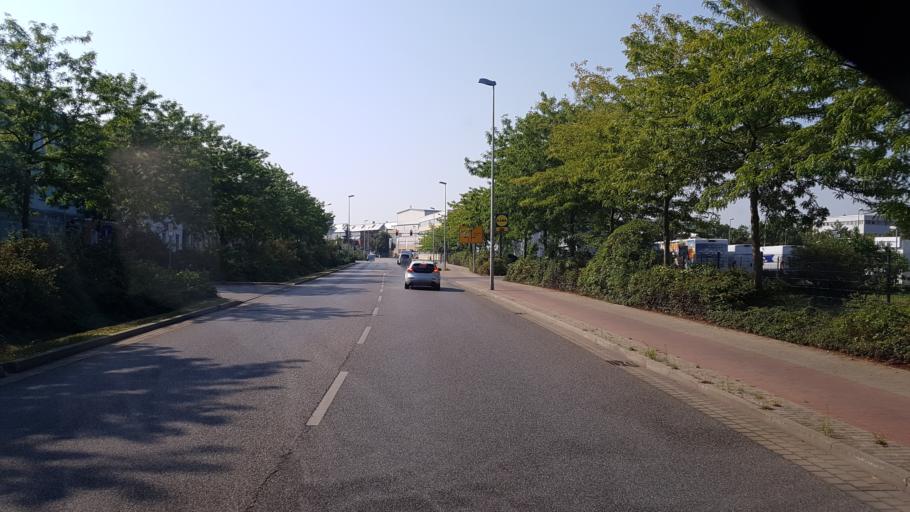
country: DE
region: Brandenburg
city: Cottbus
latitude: 51.7579
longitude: 14.3144
